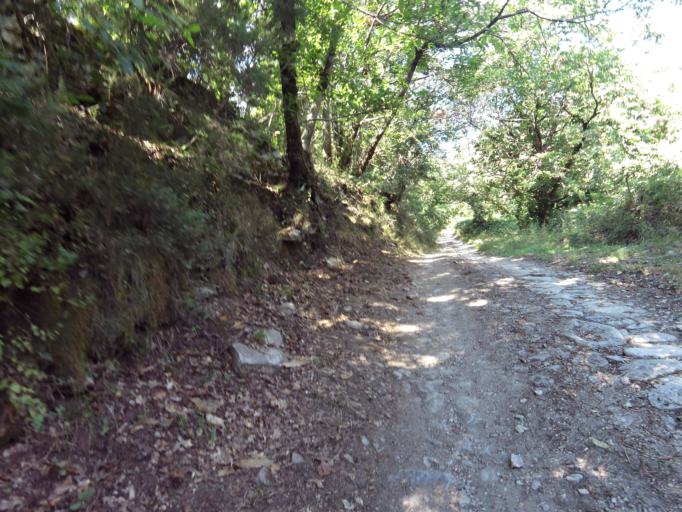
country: IT
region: Calabria
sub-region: Provincia di Reggio Calabria
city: Bivongi
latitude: 38.4878
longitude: 16.4184
